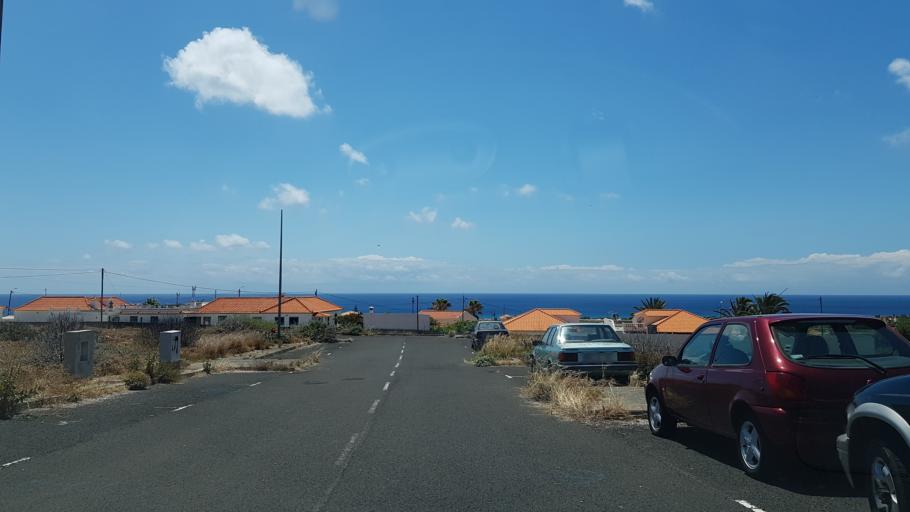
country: PT
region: Madeira
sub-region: Porto Santo
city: Vila de Porto Santo
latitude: 33.0560
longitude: -16.3586
